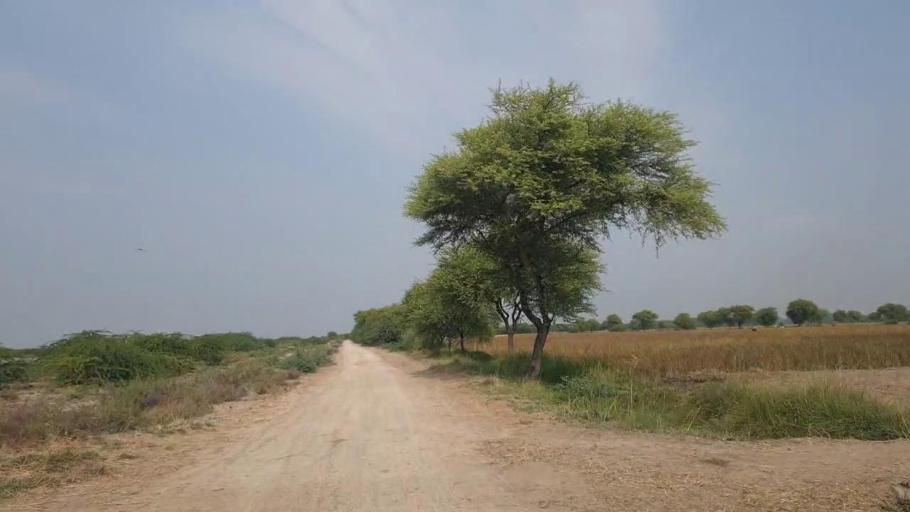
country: PK
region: Sindh
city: Badin
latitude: 24.5610
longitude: 68.7330
